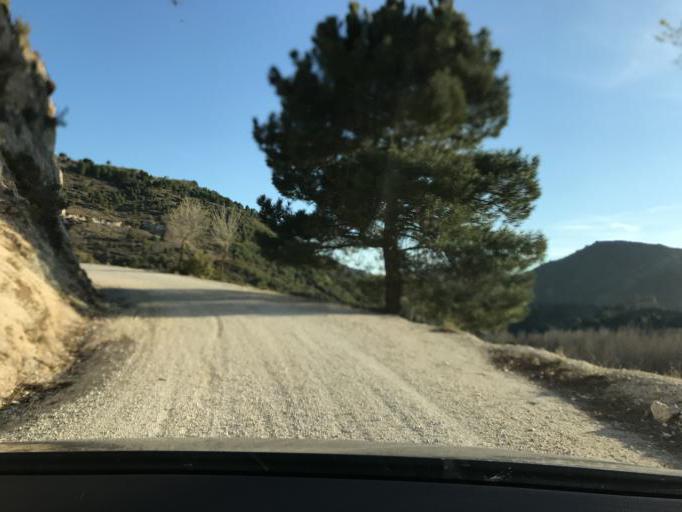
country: ES
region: Andalusia
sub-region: Provincia de Granada
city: Quentar
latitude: 37.2347
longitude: -3.4043
